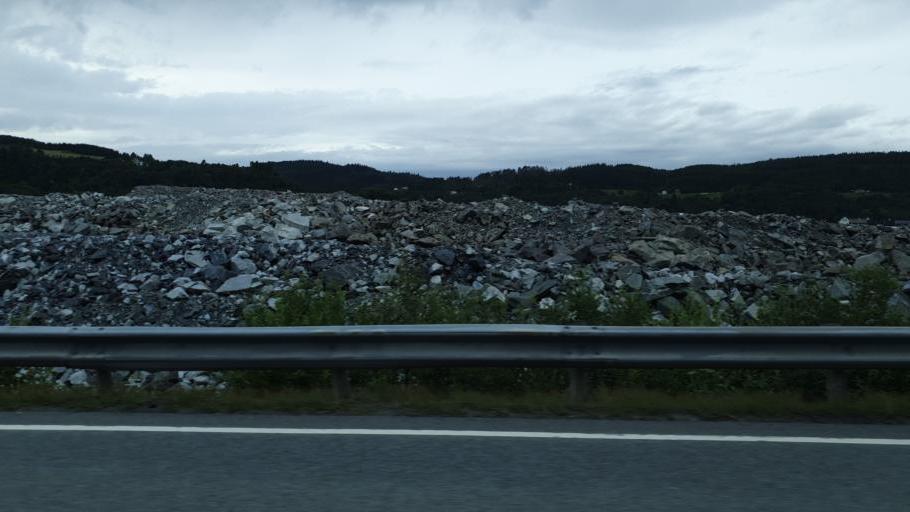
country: NO
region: Sor-Trondelag
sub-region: Melhus
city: Lundamo
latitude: 63.1062
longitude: 10.2361
